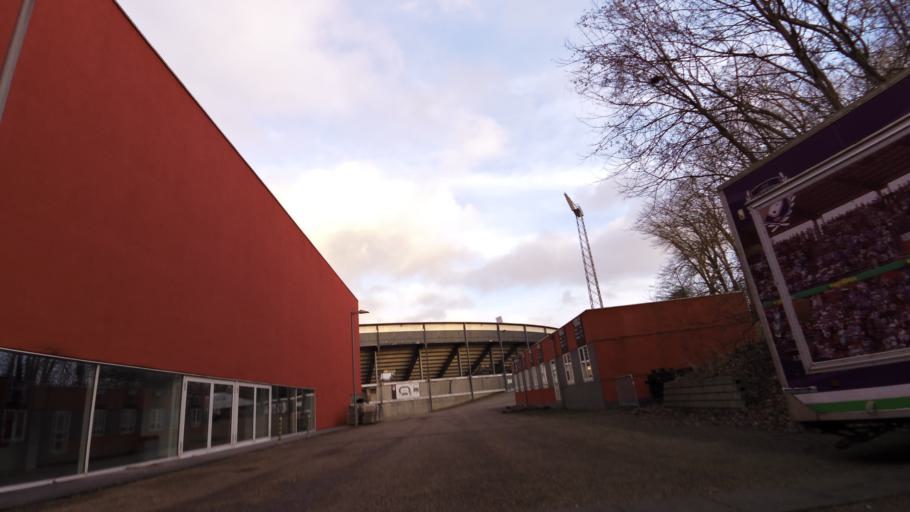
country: DK
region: Central Jutland
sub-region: Arhus Kommune
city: Arhus
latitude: 56.1315
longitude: 10.1938
